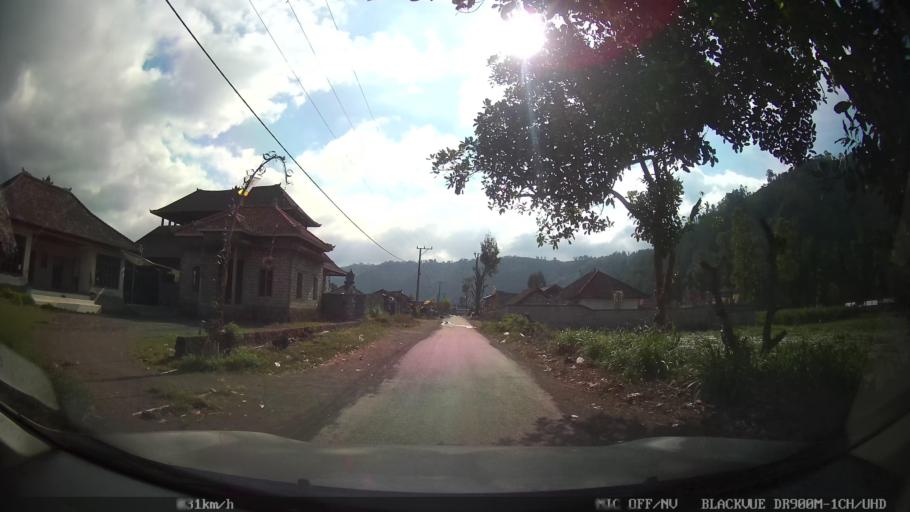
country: ID
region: Bali
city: Banjar Trunyan
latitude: -8.2154
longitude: 115.3787
